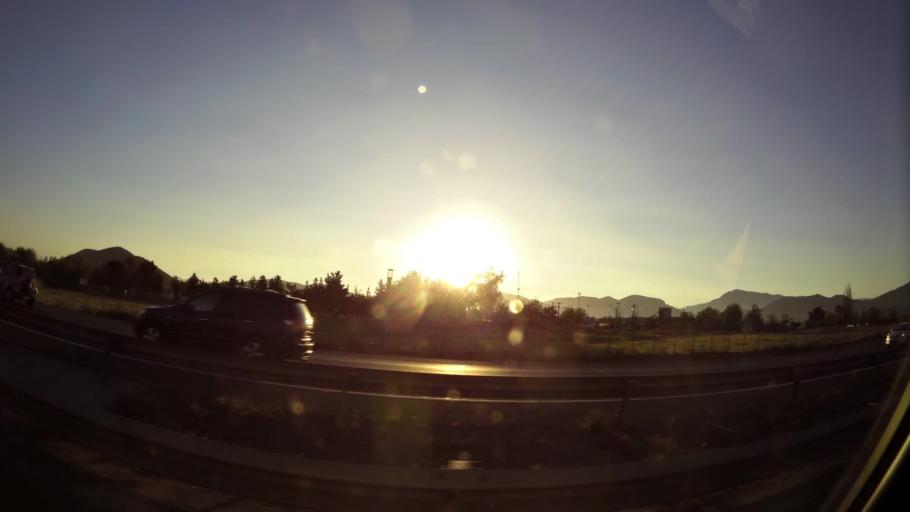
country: CL
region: Santiago Metropolitan
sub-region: Provincia de Santiago
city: Lo Prado
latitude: -33.5228
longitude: -70.7990
